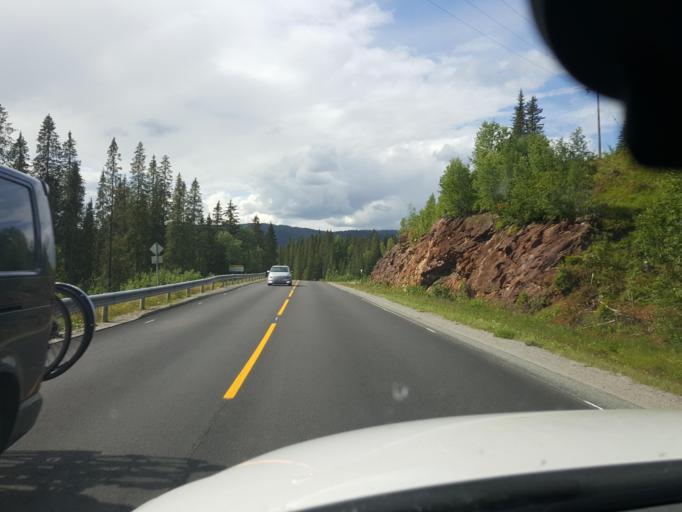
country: NO
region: Nordland
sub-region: Rana
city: Mo i Rana
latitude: 66.4075
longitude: 14.5199
